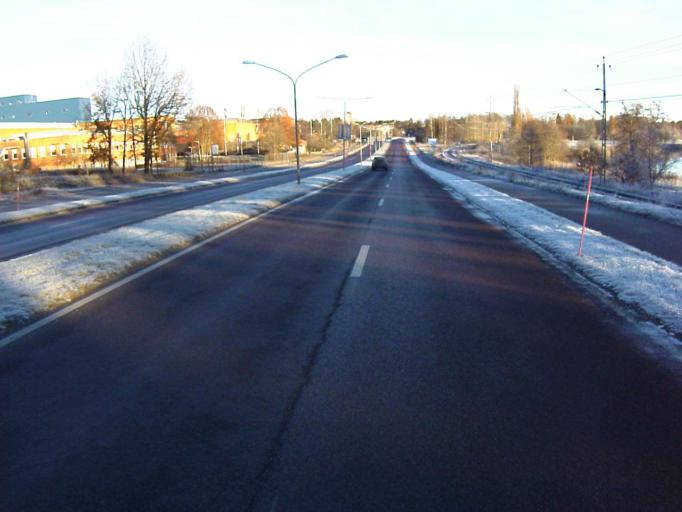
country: SE
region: Soedermanland
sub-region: Eskilstuna Kommun
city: Eskilstuna
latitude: 59.3480
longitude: 16.4949
